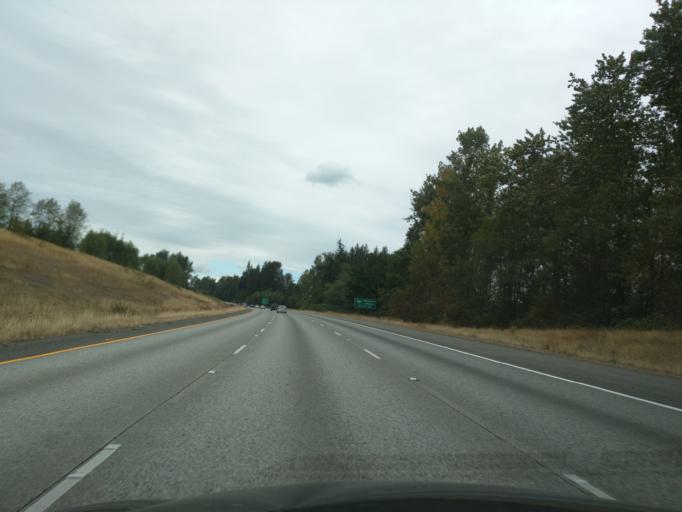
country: US
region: Washington
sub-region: Snohomish County
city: Bryant
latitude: 48.2229
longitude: -122.2216
